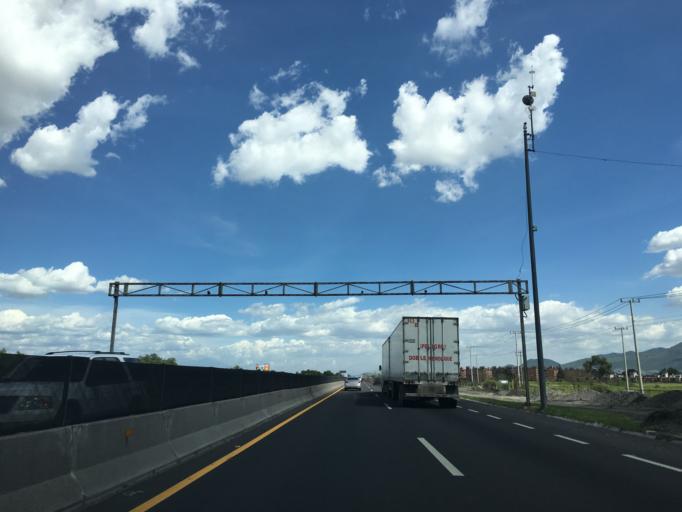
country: MX
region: Mexico
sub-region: Tonanitla
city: Colonia la Asuncion
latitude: 19.6894
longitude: -99.0779
